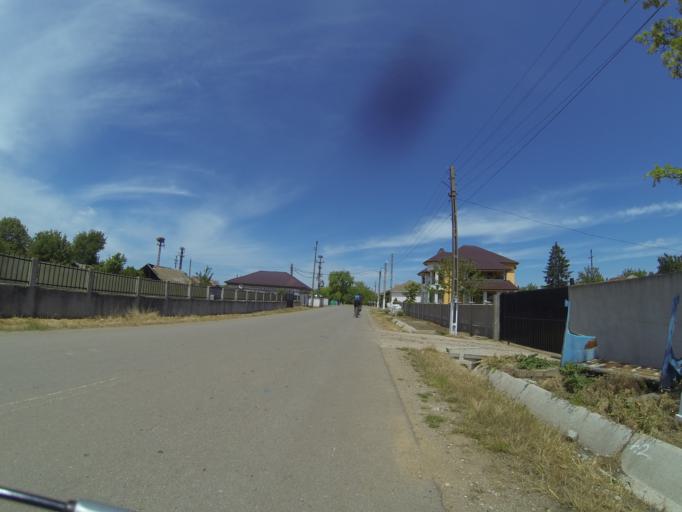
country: RO
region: Dolj
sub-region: Comuna Diosti
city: Radomir
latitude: 44.1594
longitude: 24.1626
